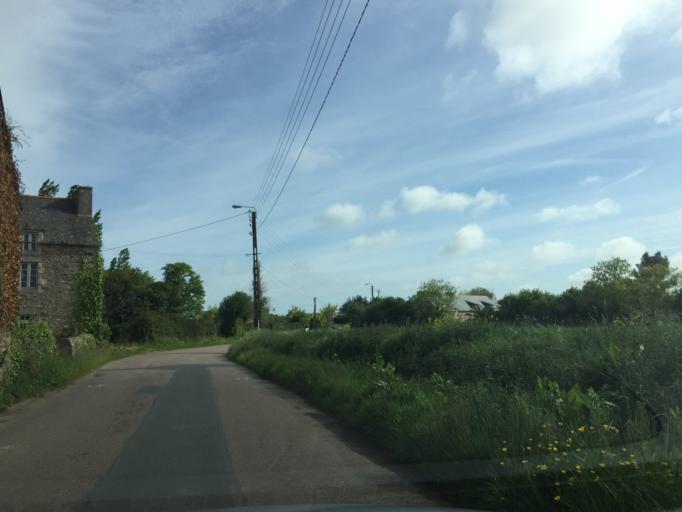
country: FR
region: Brittany
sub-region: Departement des Cotes-d'Armor
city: Plurien
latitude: 48.6220
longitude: -2.3464
